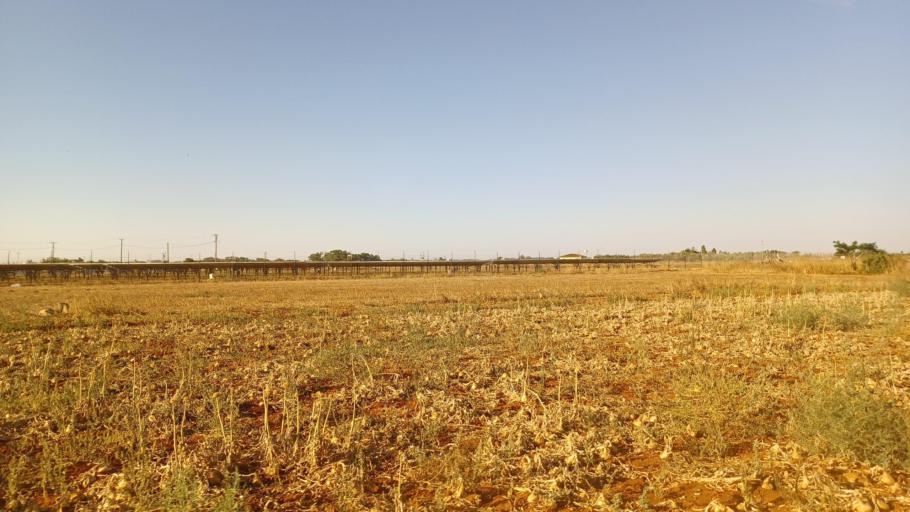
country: CY
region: Ammochostos
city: Achna
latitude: 35.0552
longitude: 33.7997
